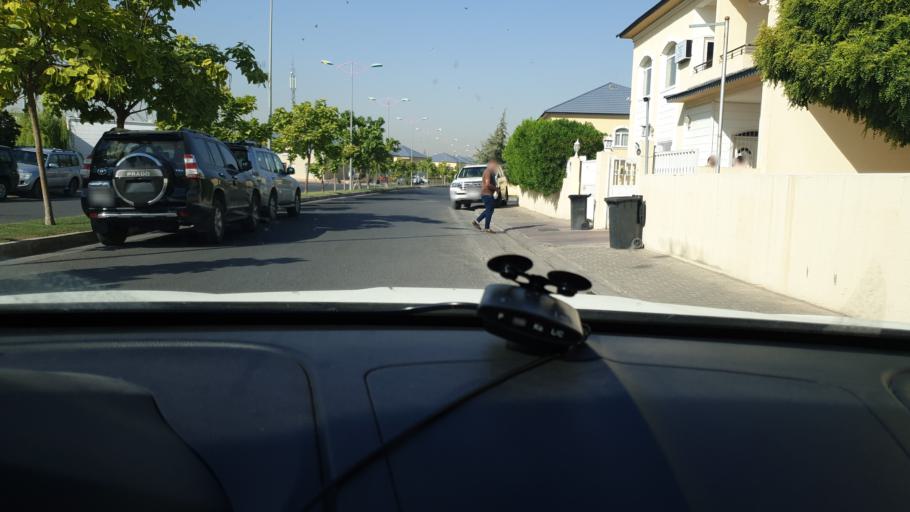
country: IQ
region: Arbil
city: Erbil
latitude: 36.1889
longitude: 43.9698
